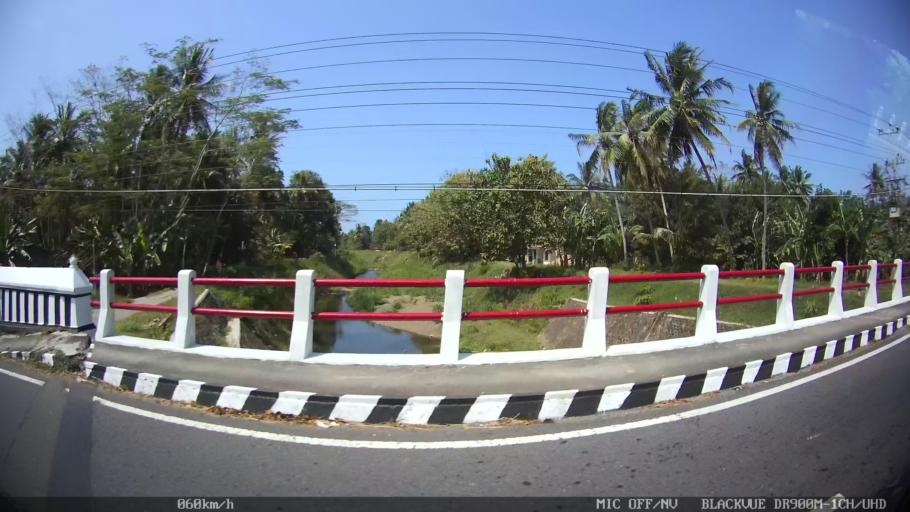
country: ID
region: Daerah Istimewa Yogyakarta
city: Srandakan
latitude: -7.8902
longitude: 110.1069
